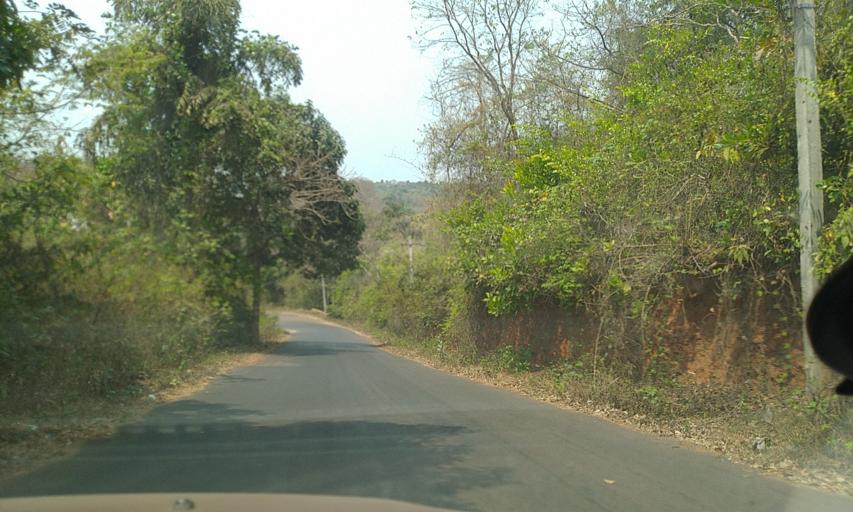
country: IN
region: Goa
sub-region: North Goa
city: Goa Velha
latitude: 15.4790
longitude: 73.8920
